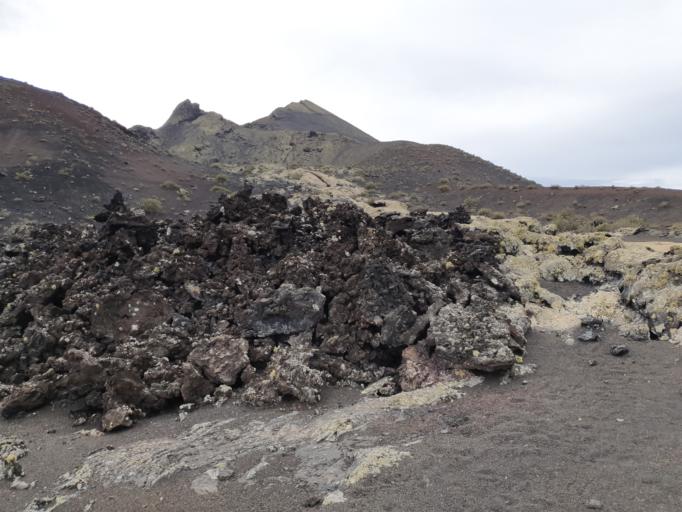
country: ES
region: Canary Islands
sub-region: Provincia de Las Palmas
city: Tinajo
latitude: 29.0127
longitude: -13.7181
